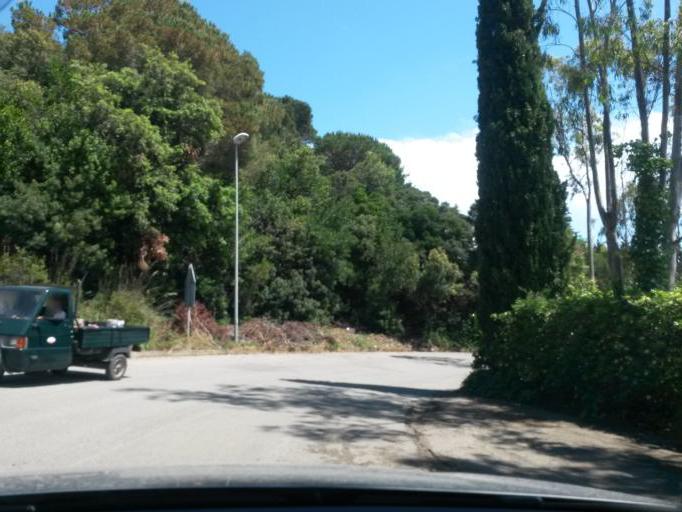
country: IT
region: Tuscany
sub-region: Provincia di Livorno
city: Rio Marina
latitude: 42.8577
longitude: 10.4143
